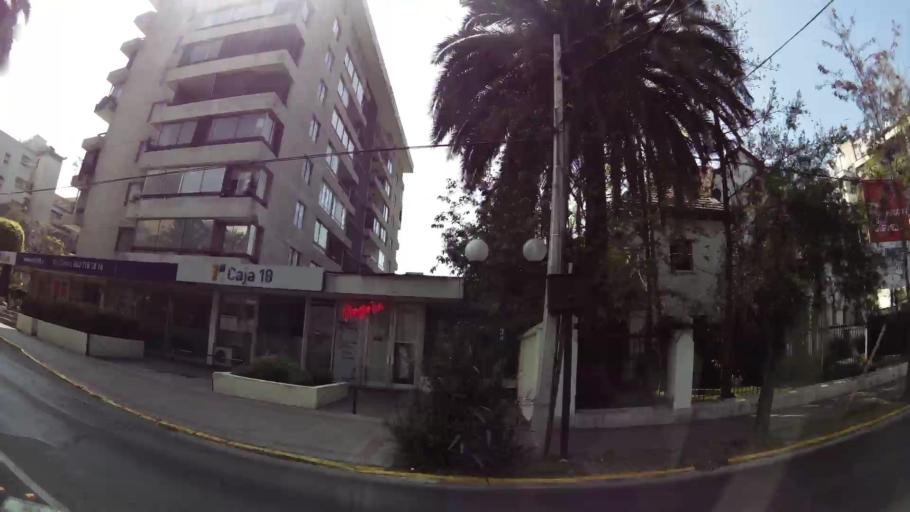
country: CL
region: Santiago Metropolitan
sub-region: Provincia de Santiago
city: Villa Presidente Frei, Nunoa, Santiago, Chile
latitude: -33.4231
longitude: -70.6069
